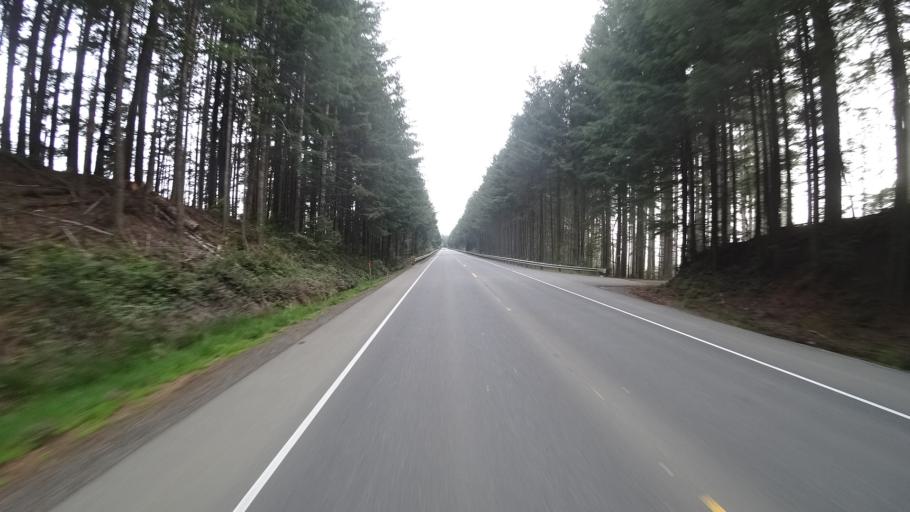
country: US
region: Oregon
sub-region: Coos County
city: Barview
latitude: 43.2440
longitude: -124.2878
